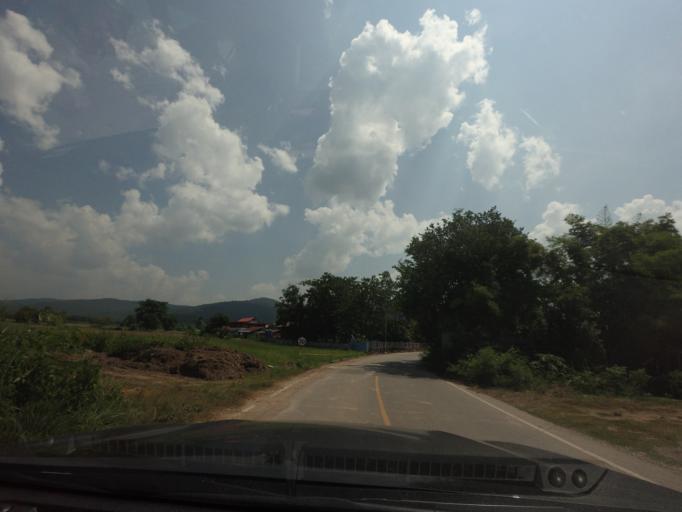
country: TH
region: Uttaradit
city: Thong Saen Khan
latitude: 17.4270
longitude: 100.3250
